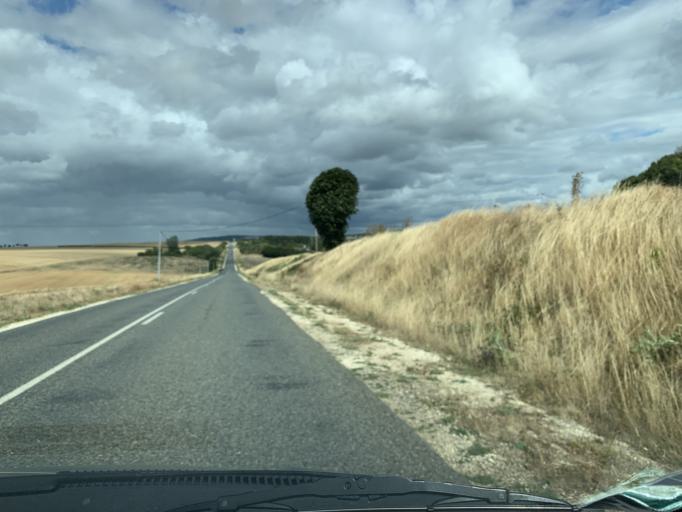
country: FR
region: Bourgogne
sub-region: Departement de la Nievre
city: Clamecy
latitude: 47.4300
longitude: 3.4785
